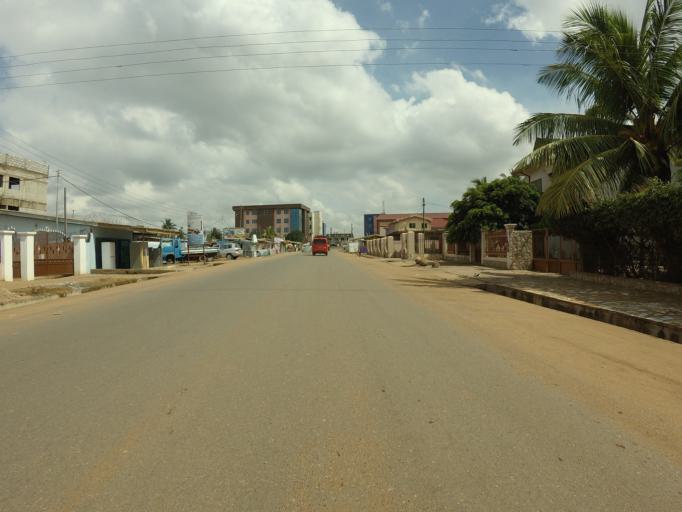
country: GH
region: Greater Accra
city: Nungua
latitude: 5.6284
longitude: -0.0927
